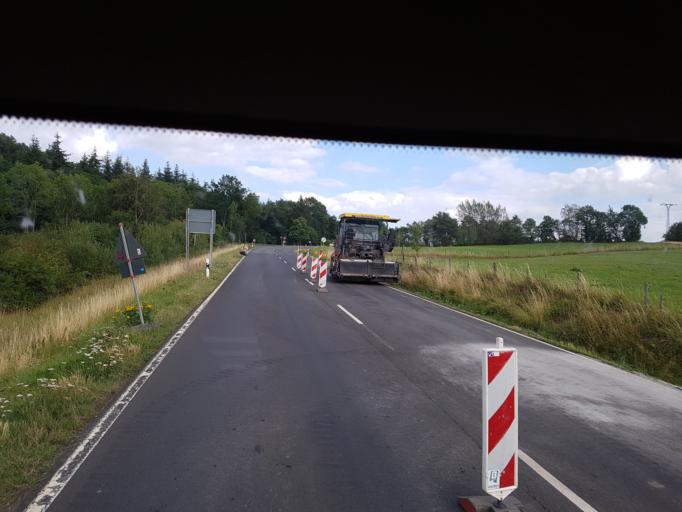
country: DE
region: Rheinland-Pfalz
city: Betteldorf
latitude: 50.2506
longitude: 6.7571
